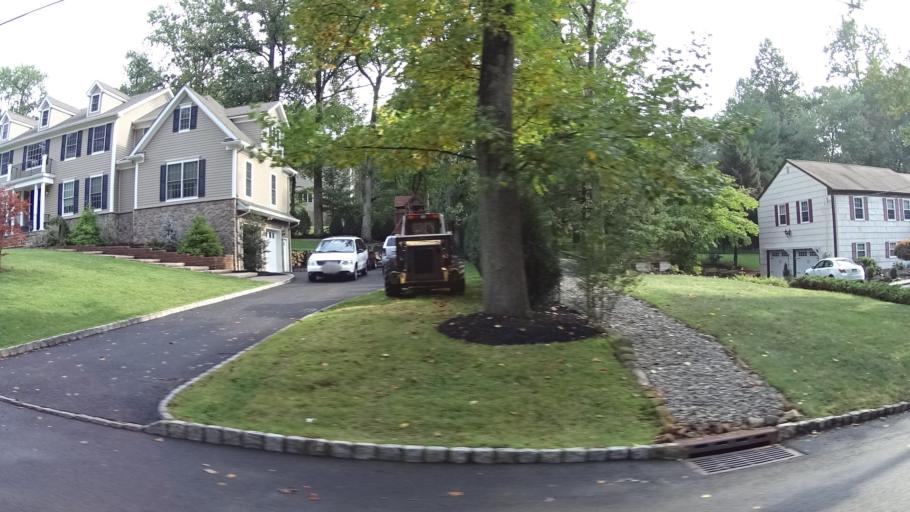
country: US
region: New Jersey
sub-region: Union County
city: Berkeley Heights
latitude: 40.7067
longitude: -74.4324
